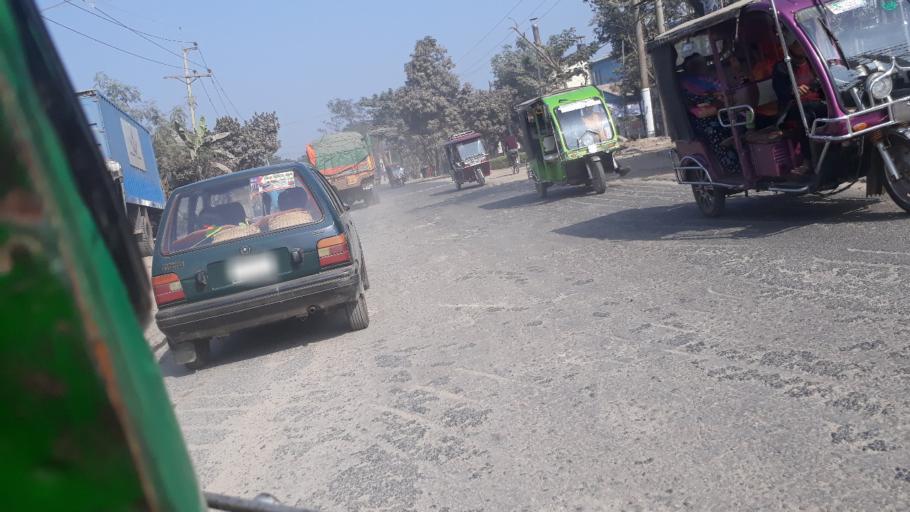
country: BD
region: Khulna
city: Kushtia
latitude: 23.8871
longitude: 89.1070
